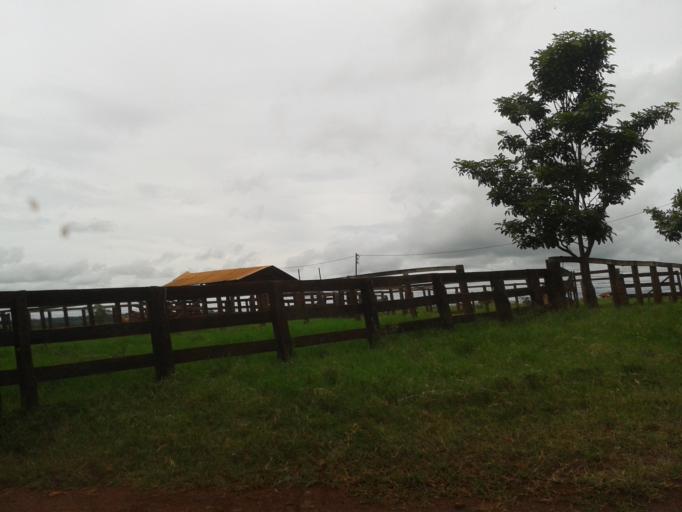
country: BR
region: Minas Gerais
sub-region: Capinopolis
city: Capinopolis
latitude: -18.7954
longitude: -49.7859
